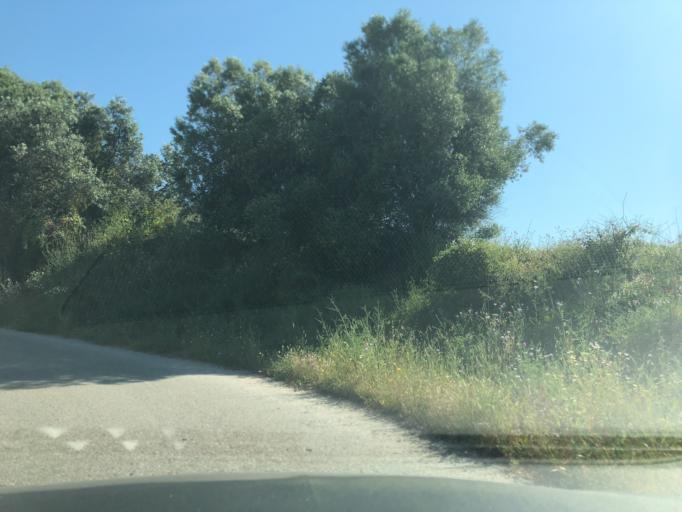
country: PT
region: Lisbon
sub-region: Oeiras
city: Quejas
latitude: 38.7165
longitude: -9.2739
